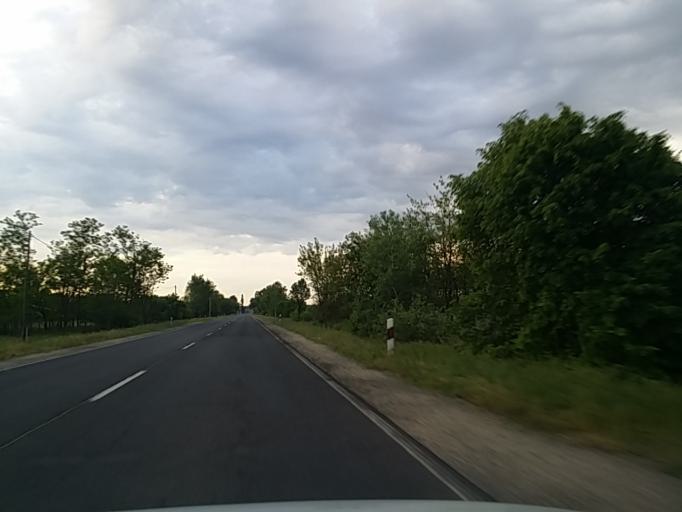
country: HU
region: Pest
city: Taborfalva
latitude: 47.0742
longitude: 19.4938
